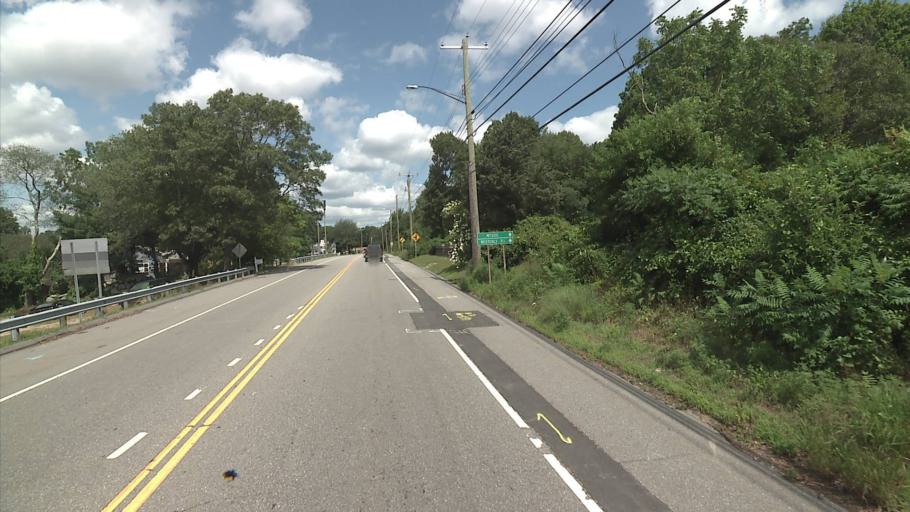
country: US
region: Connecticut
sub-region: New London County
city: Poquonock Bridge
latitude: 41.3458
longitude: -72.0115
